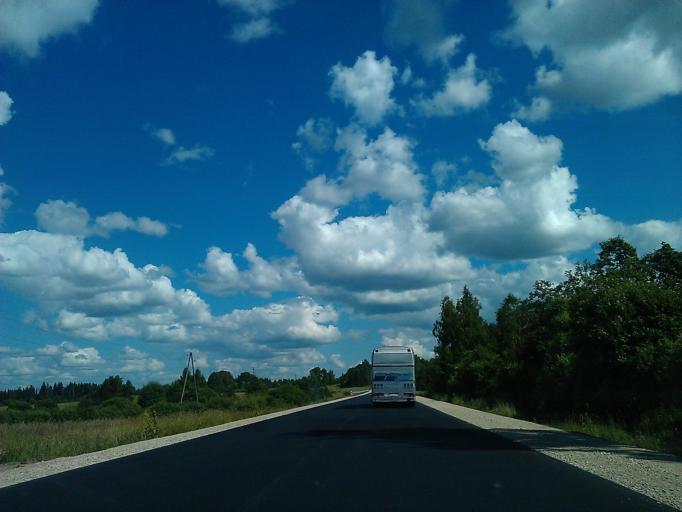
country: LV
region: Rezekne
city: Rezekne
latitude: 56.5381
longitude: 27.1572
